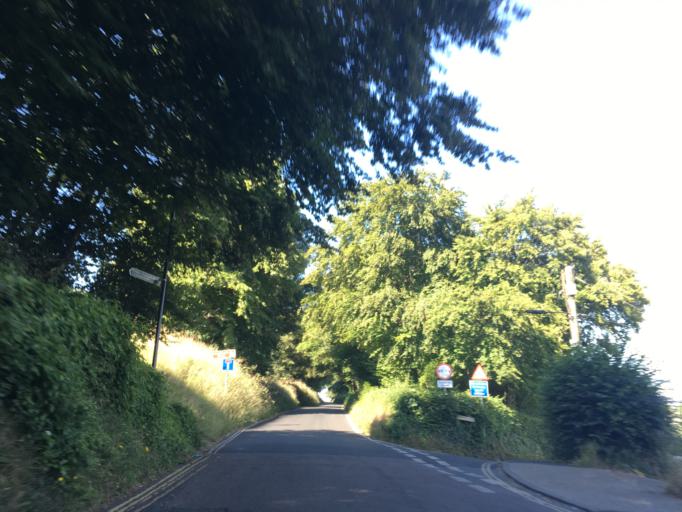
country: GB
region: England
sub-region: Isle of Wight
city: Newport
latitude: 50.6895
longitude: -1.3111
